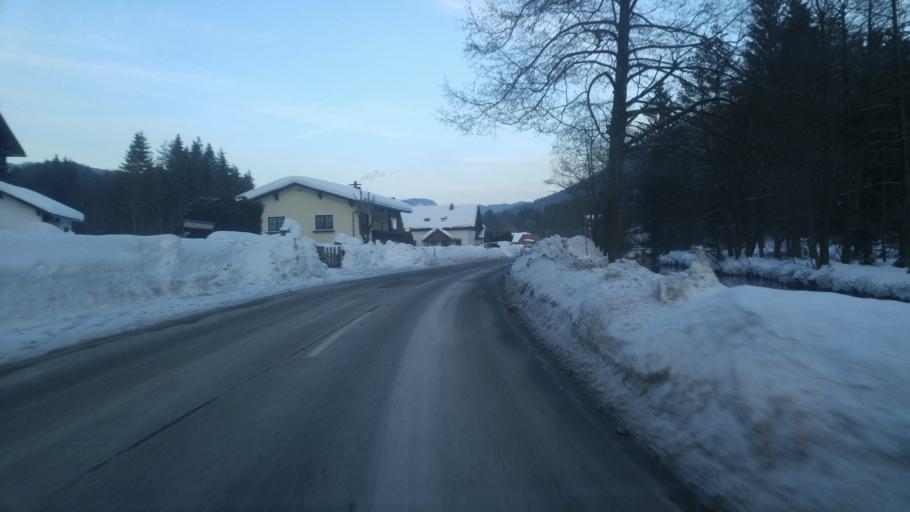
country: AT
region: Lower Austria
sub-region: Politischer Bezirk Wiener Neustadt
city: Rohr im Gebirge
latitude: 47.8794
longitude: 15.7074
